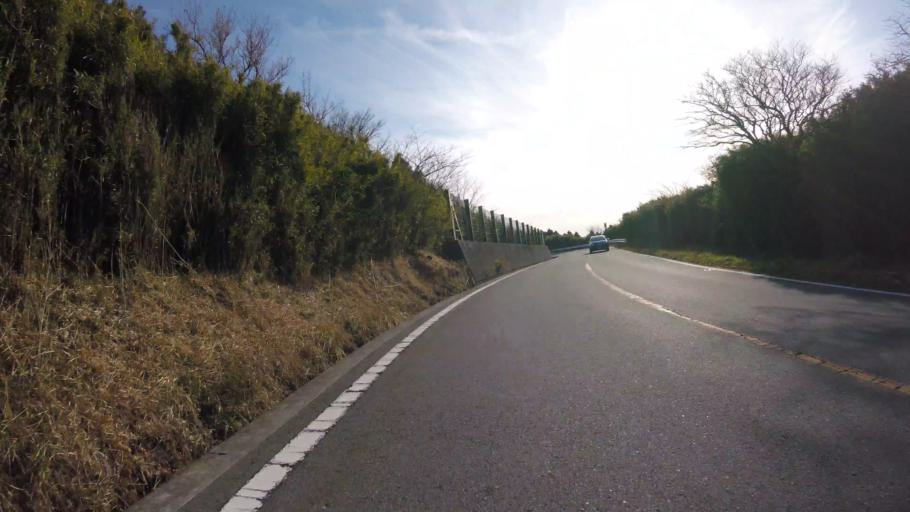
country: JP
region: Kanagawa
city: Yugawara
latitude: 35.1364
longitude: 139.0374
